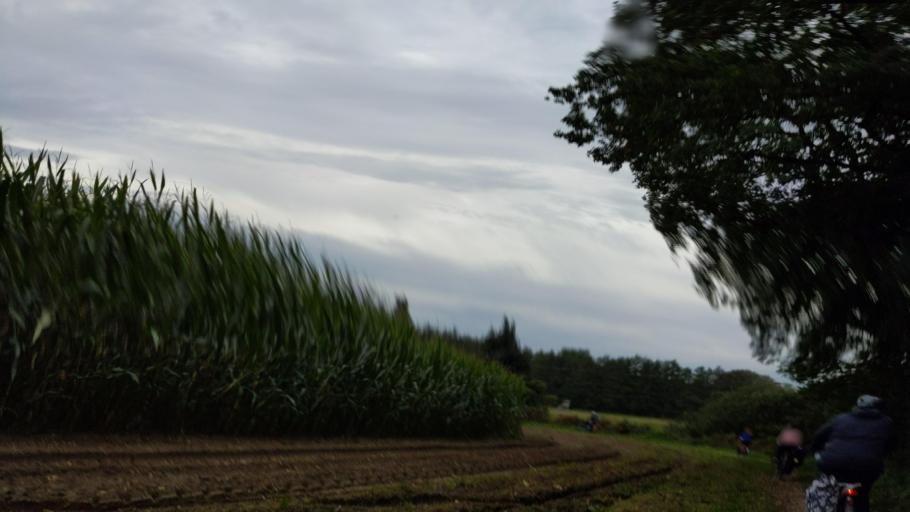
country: DE
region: Schleswig-Holstein
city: Gross Gronau
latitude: 53.7863
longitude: 10.7647
